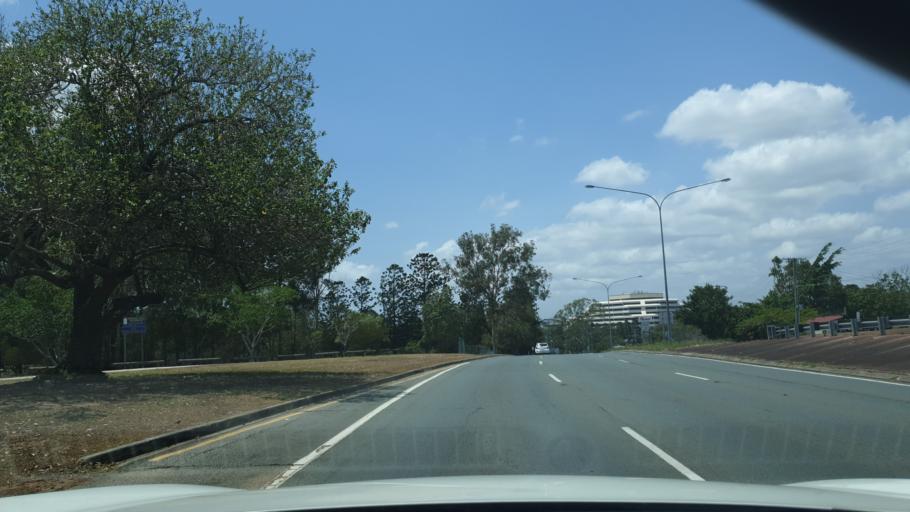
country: AU
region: Queensland
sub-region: Brisbane
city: Chermside West
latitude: -27.3764
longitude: 153.0275
